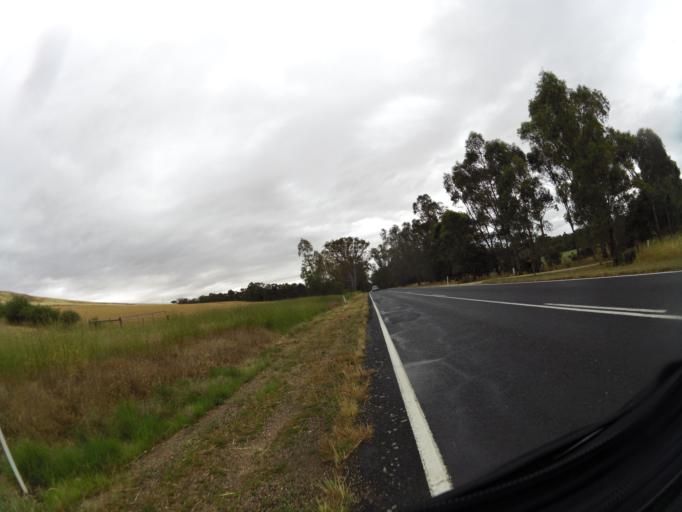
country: AU
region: Victoria
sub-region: Mount Alexander
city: Castlemaine
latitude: -37.1513
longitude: 144.0414
